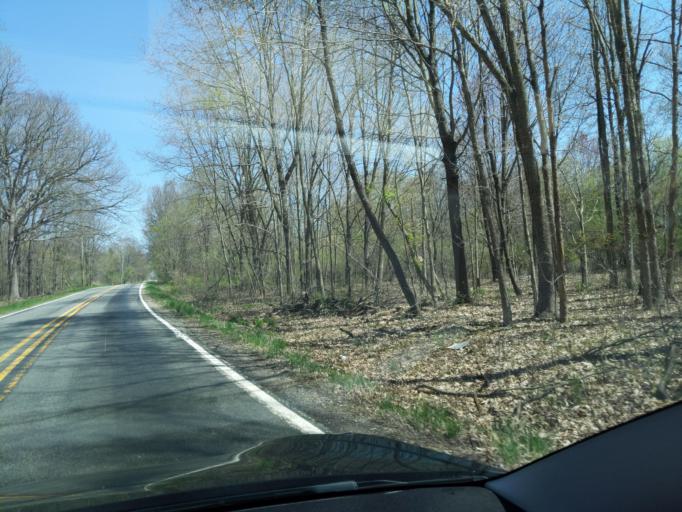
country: US
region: Michigan
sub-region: Ingham County
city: Stockbridge
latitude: 42.5033
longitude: -84.2485
